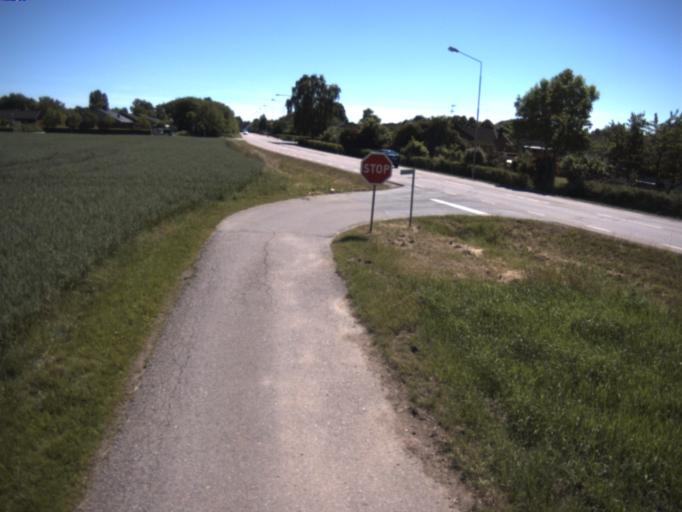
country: SE
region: Skane
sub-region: Helsingborg
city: Morarp
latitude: 56.0628
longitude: 12.8796
